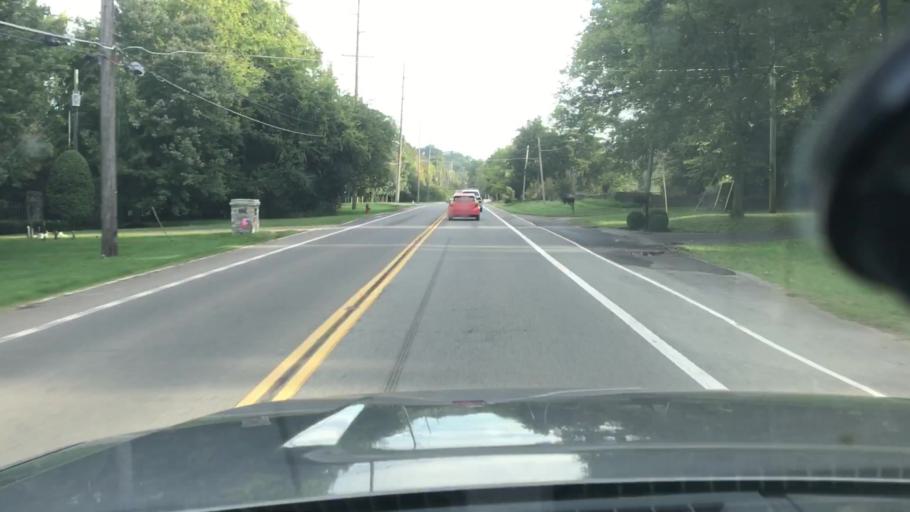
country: US
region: Tennessee
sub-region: Davidson County
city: Forest Hills
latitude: 36.0711
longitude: -86.8420
